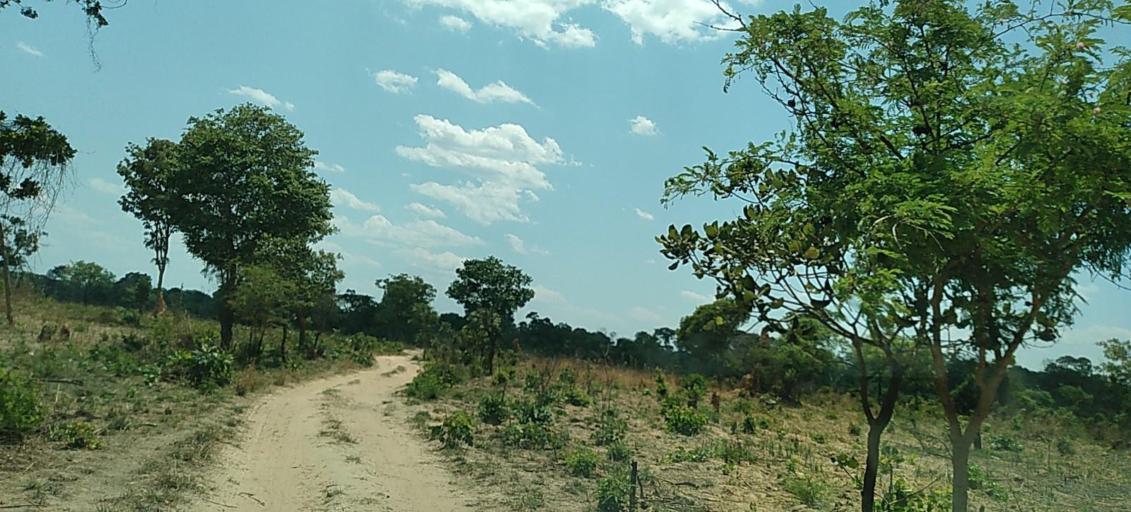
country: ZM
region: Central
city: Kapiri Mposhi
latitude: -13.6340
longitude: 28.7533
